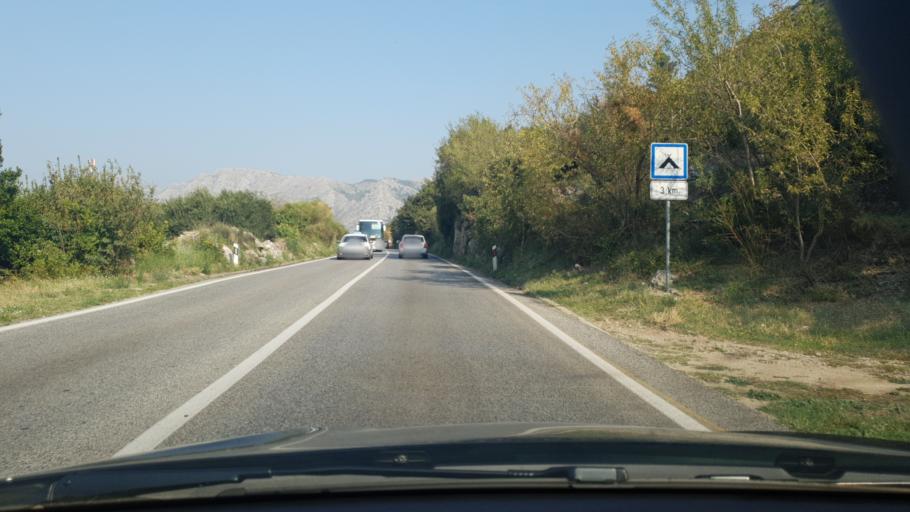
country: HR
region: Dubrovacko-Neretvanska
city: Cavtat
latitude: 42.5906
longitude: 18.2300
